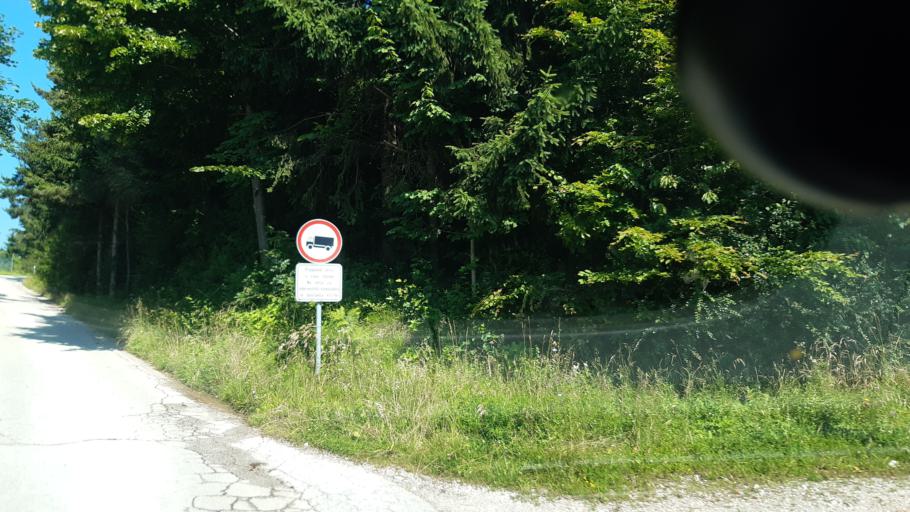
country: SI
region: Trzic
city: Bistrica pri Trzicu
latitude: 46.3590
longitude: 14.2761
